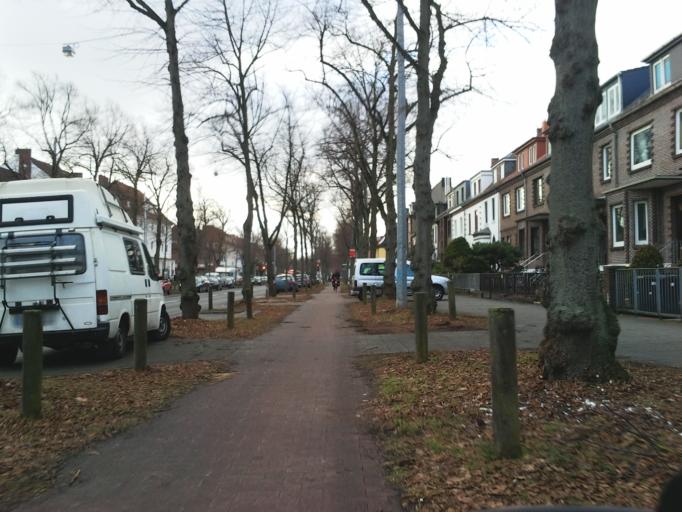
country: DE
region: Bremen
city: Bremen
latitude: 53.1017
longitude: 8.7832
